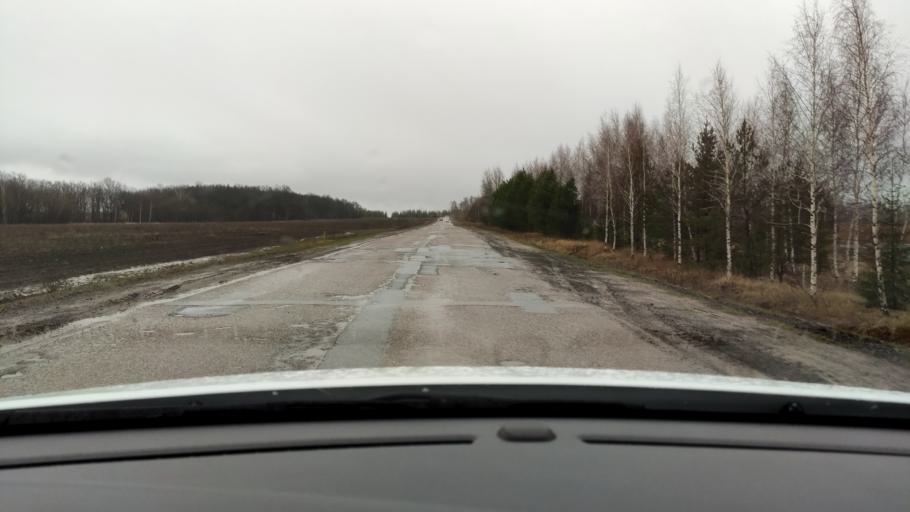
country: RU
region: Tatarstan
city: Vysokaya Gora
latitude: 55.8991
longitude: 49.3276
